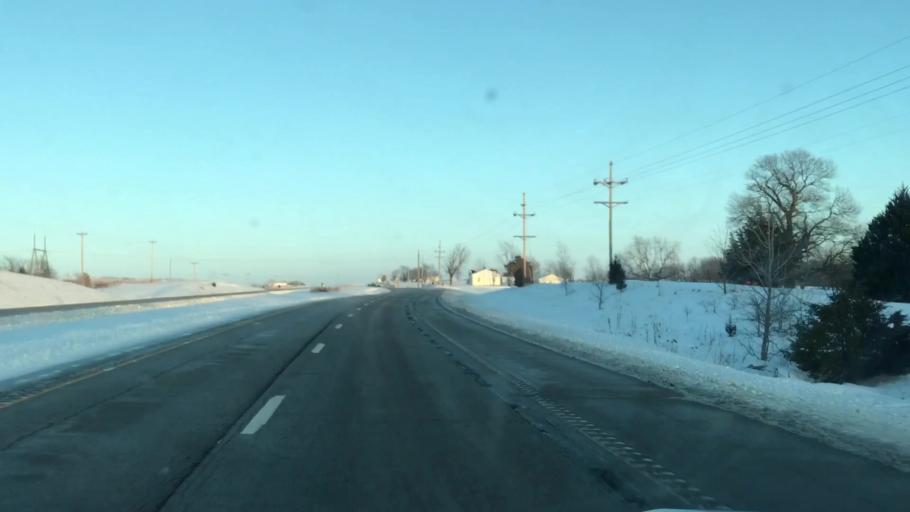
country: US
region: Missouri
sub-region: Clinton County
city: Cameron
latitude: 39.7548
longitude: -94.3122
